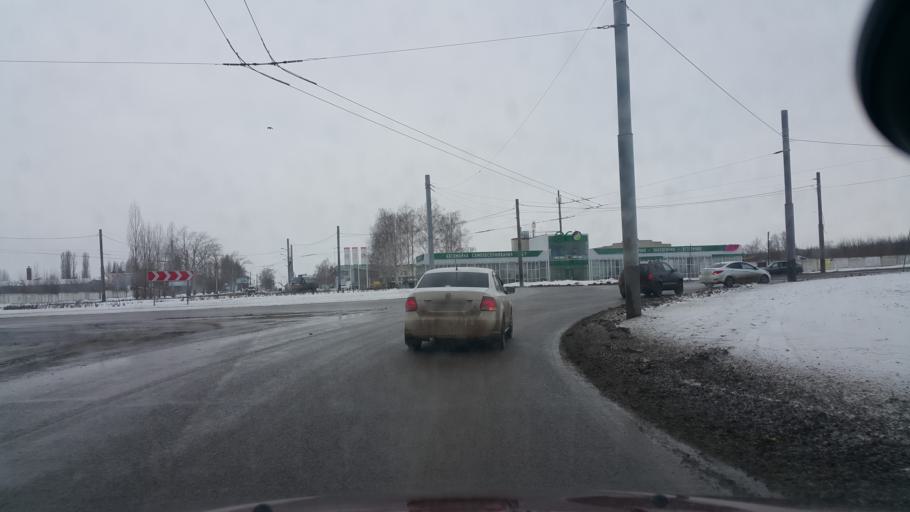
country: RU
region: Tambov
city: Tambov
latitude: 52.7385
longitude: 41.3778
